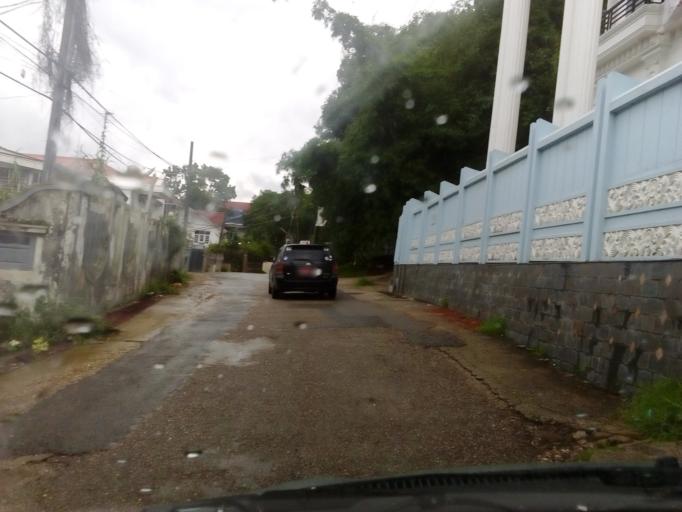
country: MM
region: Yangon
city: Yangon
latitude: 16.8184
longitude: 96.1505
